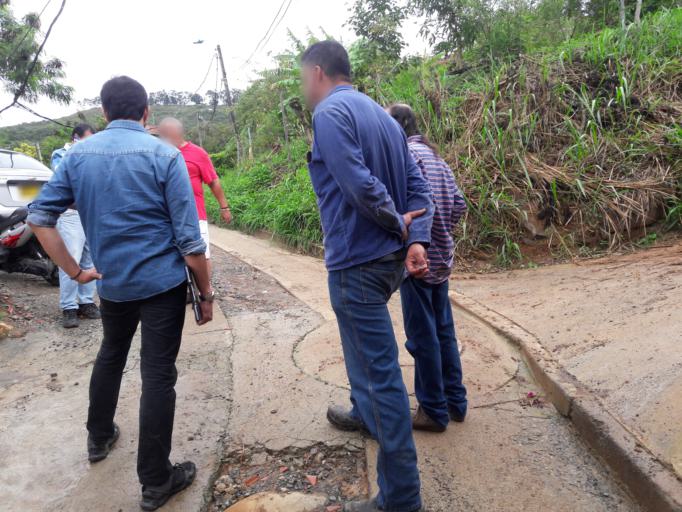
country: CO
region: Valle del Cauca
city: Cali
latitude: 3.4737
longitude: -76.5557
